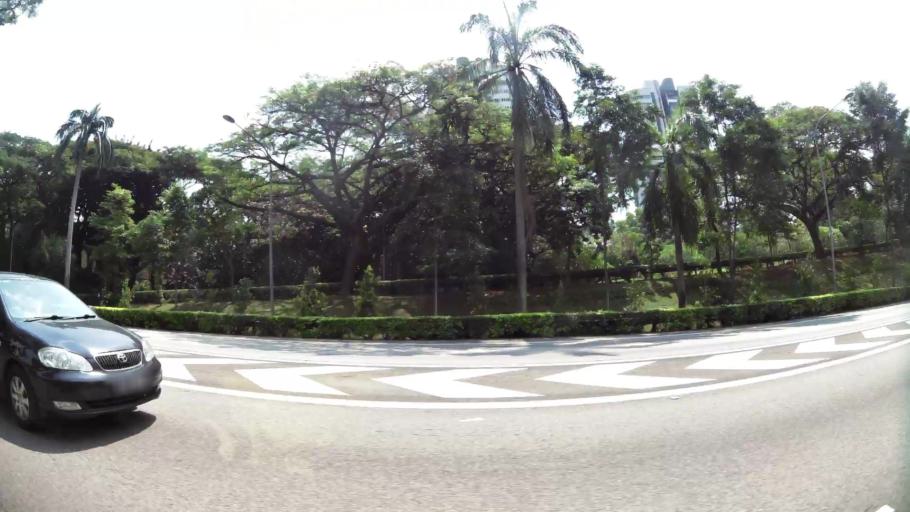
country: SG
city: Singapore
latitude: 1.2778
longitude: 103.8251
